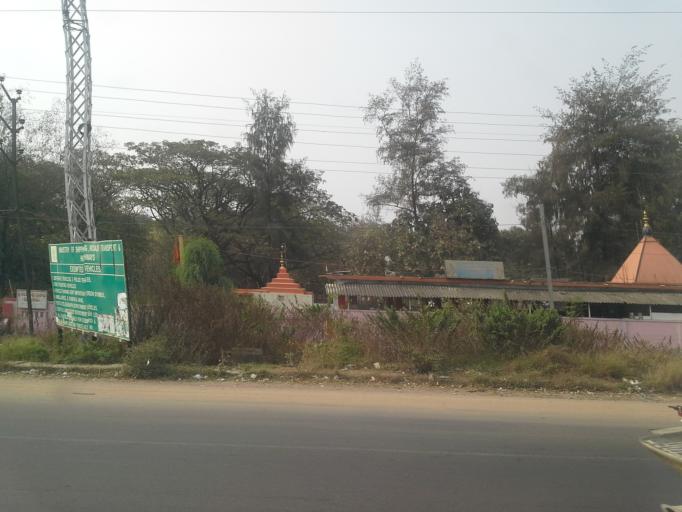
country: IN
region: Telangana
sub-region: Medak
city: Patancheru
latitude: 17.5216
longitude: 78.2754
